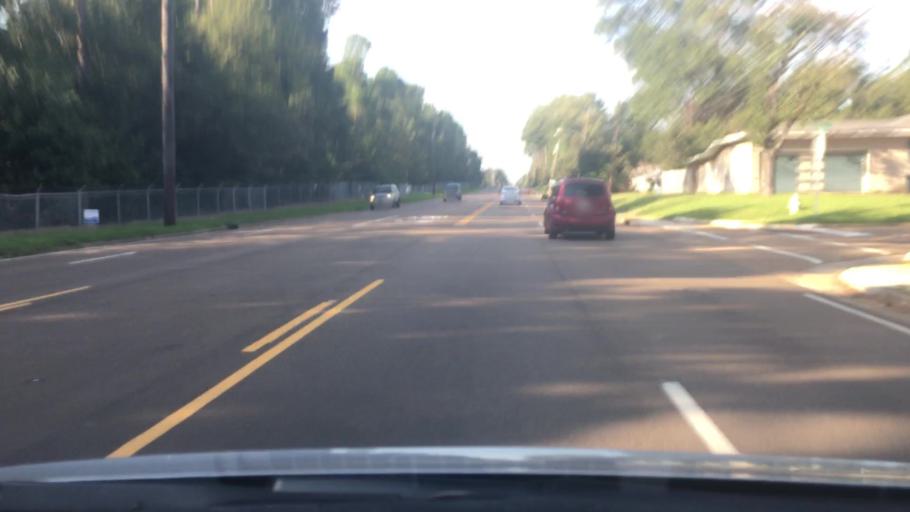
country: US
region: Mississippi
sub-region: Hinds County
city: Jackson
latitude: 32.3635
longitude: -90.1927
